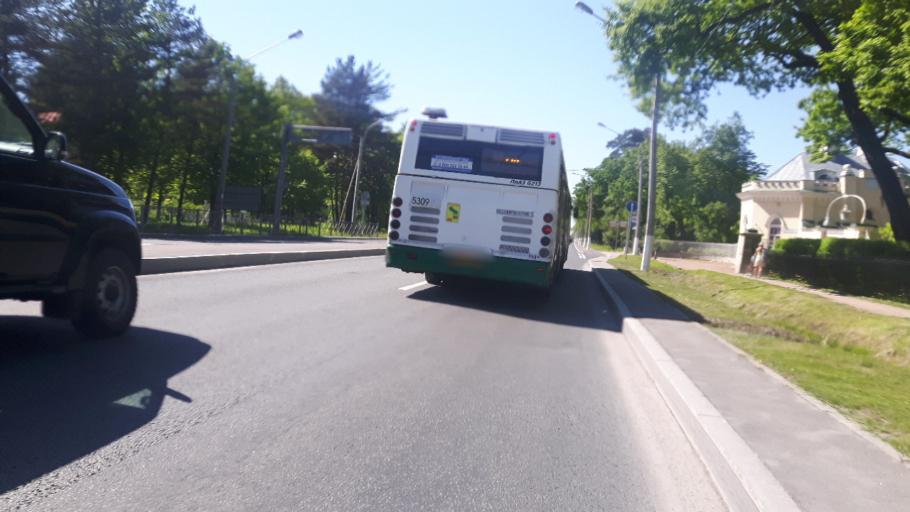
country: RU
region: Leningrad
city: Ol'gino
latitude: 59.8749
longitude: 29.9455
